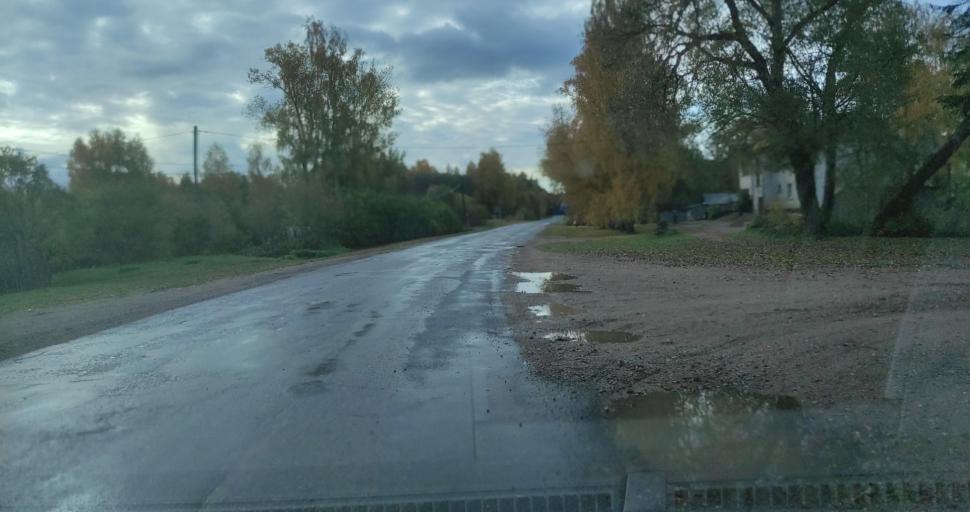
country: LV
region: Skrunda
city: Skrunda
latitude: 56.6675
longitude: 22.0230
